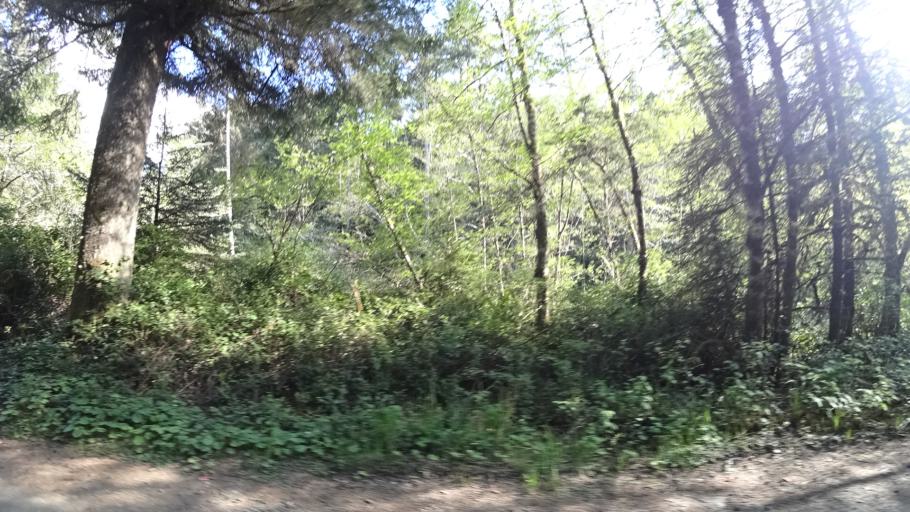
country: US
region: Oregon
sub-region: Douglas County
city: Reedsport
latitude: 43.7462
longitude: -124.1728
